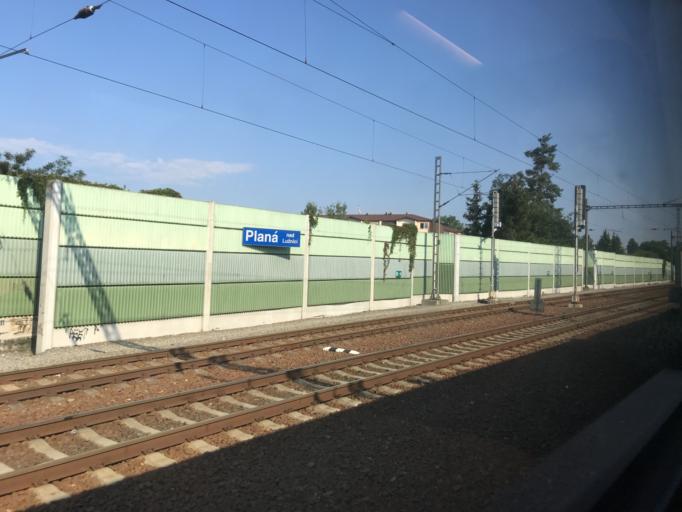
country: CZ
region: Jihocesky
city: Plana nad Luznici
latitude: 49.3505
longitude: 14.7078
